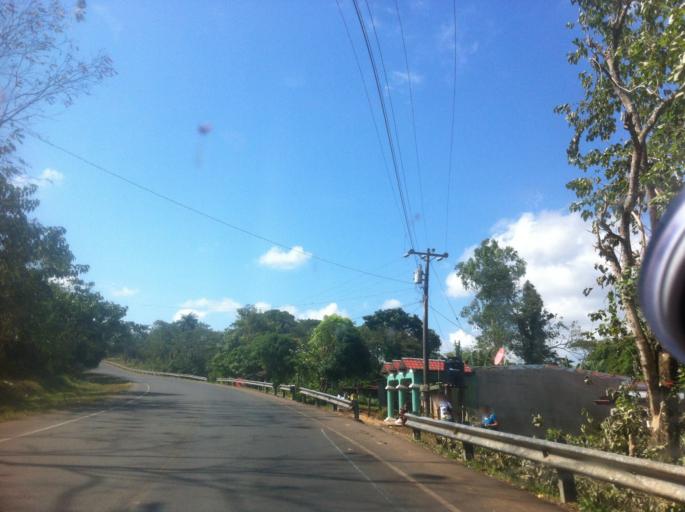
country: NI
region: Rio San Juan
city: San Carlos
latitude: 11.1875
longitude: -84.7453
